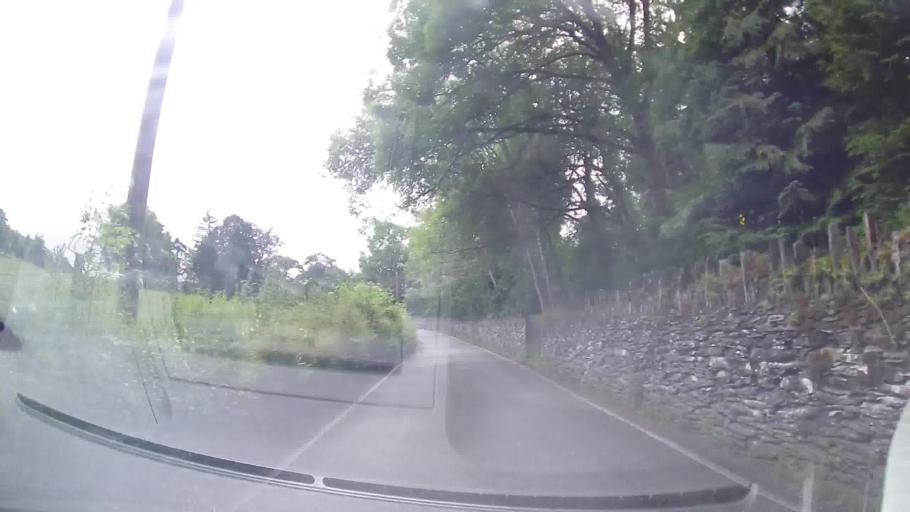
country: GB
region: Wales
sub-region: Conwy
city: Llangwm
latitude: 52.9108
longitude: -3.5158
